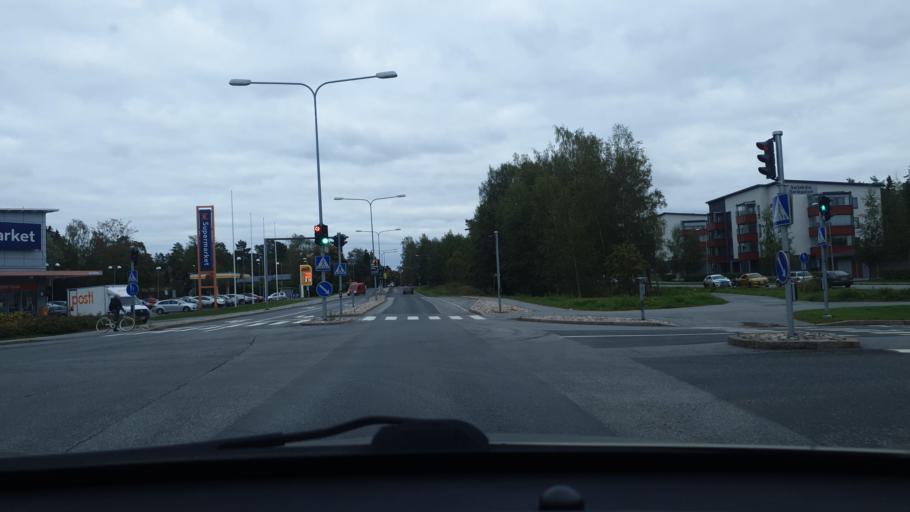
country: FI
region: Ostrobothnia
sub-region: Vaasa
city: Teeriniemi
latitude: 63.0901
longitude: 21.6827
